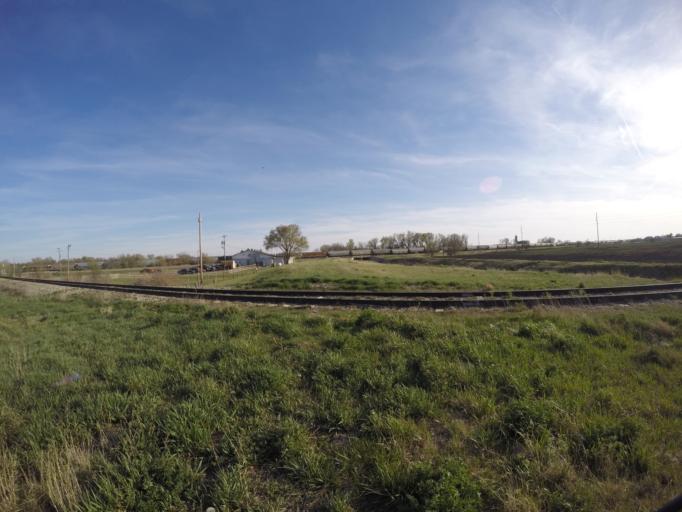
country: US
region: Kansas
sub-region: Saline County
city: Salina
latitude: 38.8454
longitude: -97.6305
